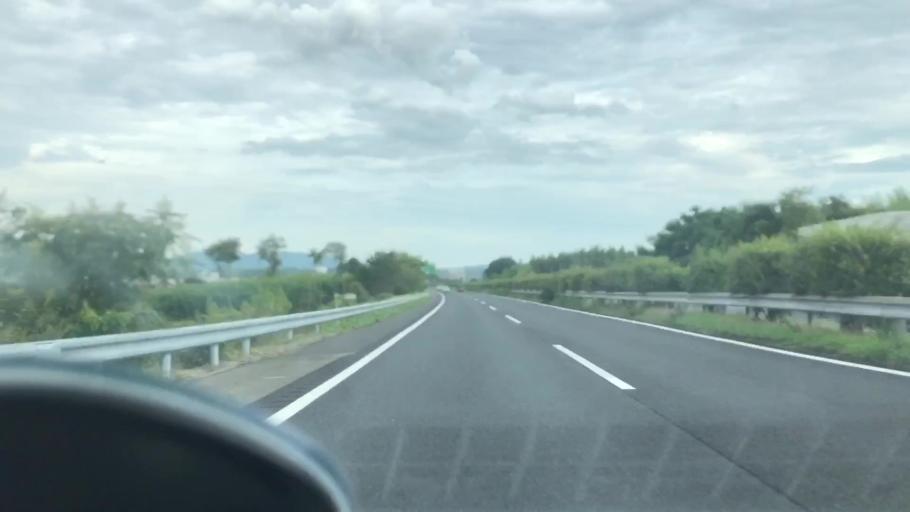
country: JP
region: Hyogo
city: Yashiro
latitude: 34.9289
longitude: 134.9459
